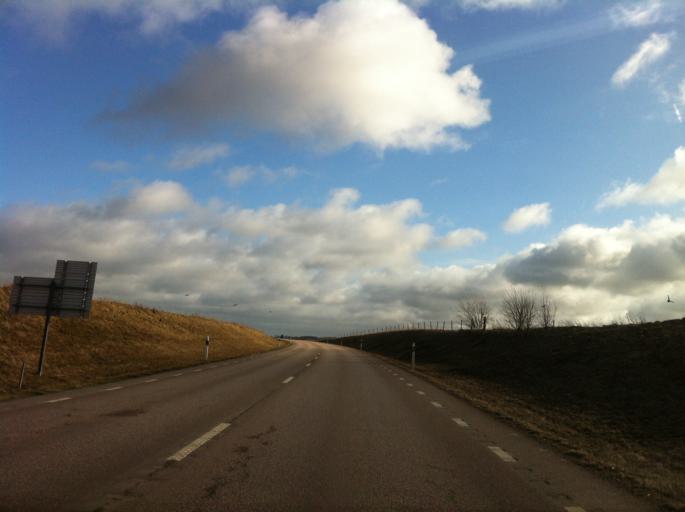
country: SE
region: Skane
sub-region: Svalovs Kommun
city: Svaloev
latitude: 55.8726
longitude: 13.1772
